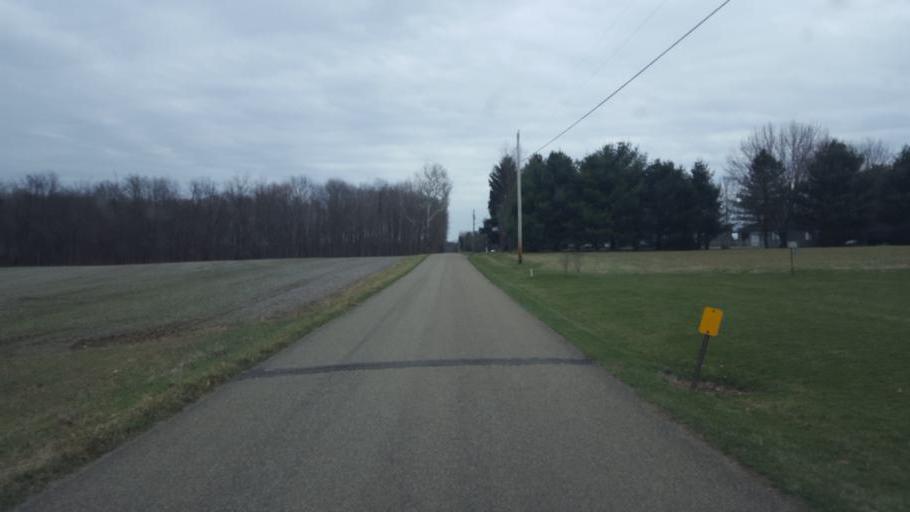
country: US
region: Ohio
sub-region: Knox County
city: Fredericktown
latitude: 40.5028
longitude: -82.5192
